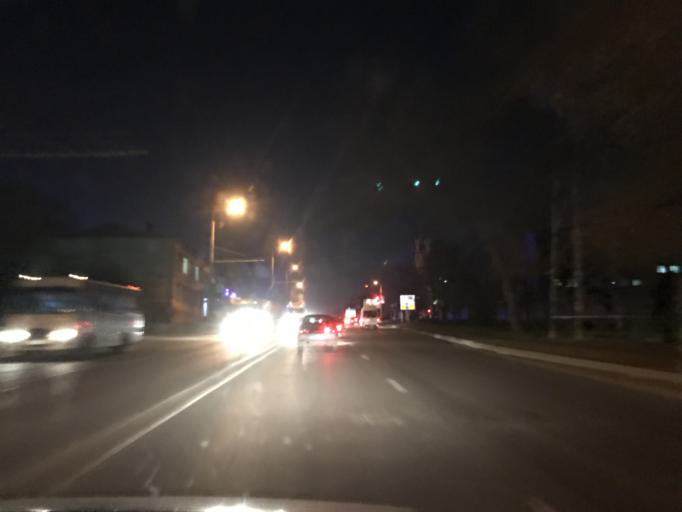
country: RU
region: Rostov
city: Kalinin
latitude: 47.2060
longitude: 39.6136
